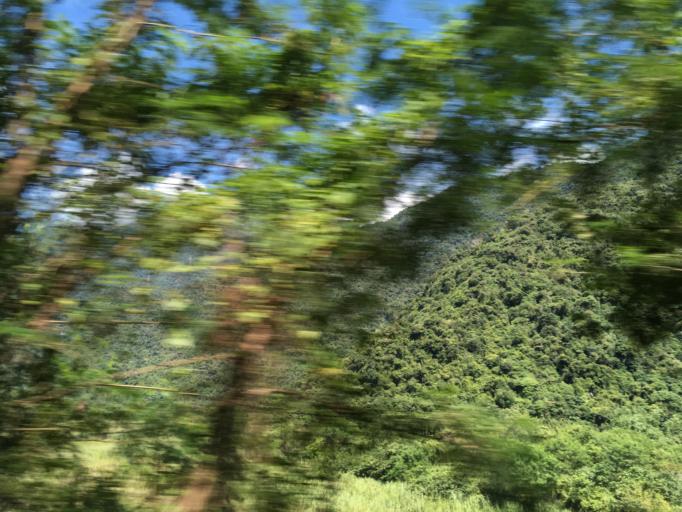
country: TW
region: Taiwan
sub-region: Yilan
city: Yilan
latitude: 24.4393
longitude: 121.7607
